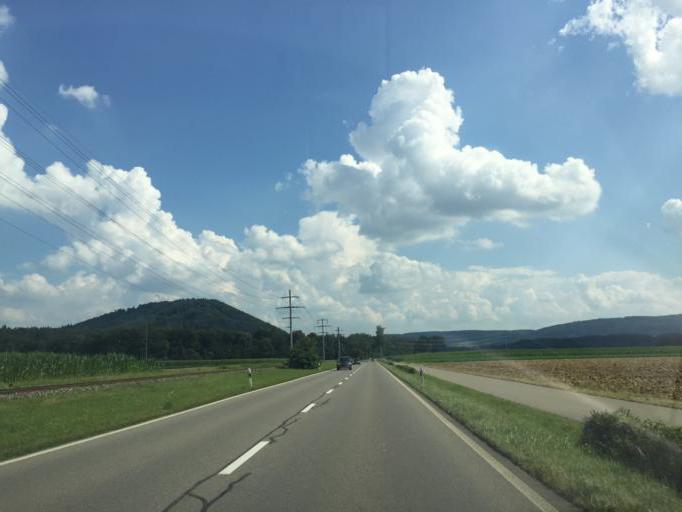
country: CH
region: Schaffhausen
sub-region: Bezirk Stein
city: Ramsen
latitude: 47.6935
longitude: 8.8257
